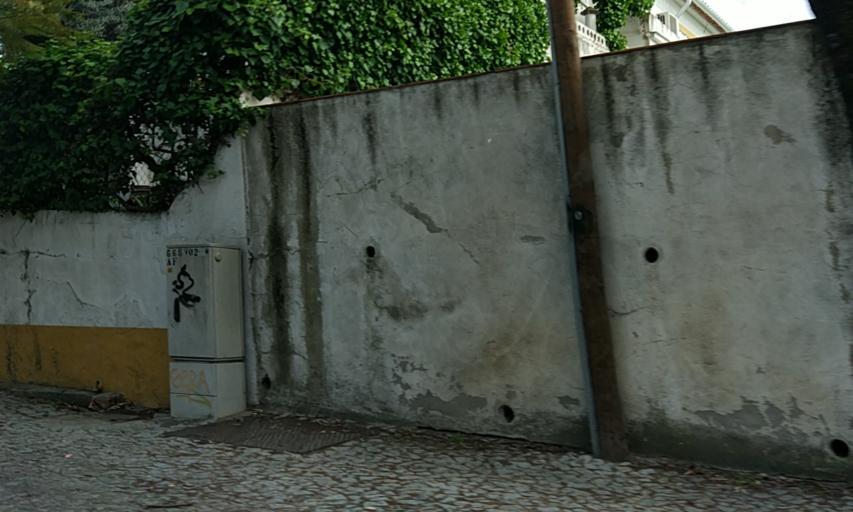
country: PT
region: Evora
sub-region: Evora
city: Evora
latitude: 38.5674
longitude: -7.9241
